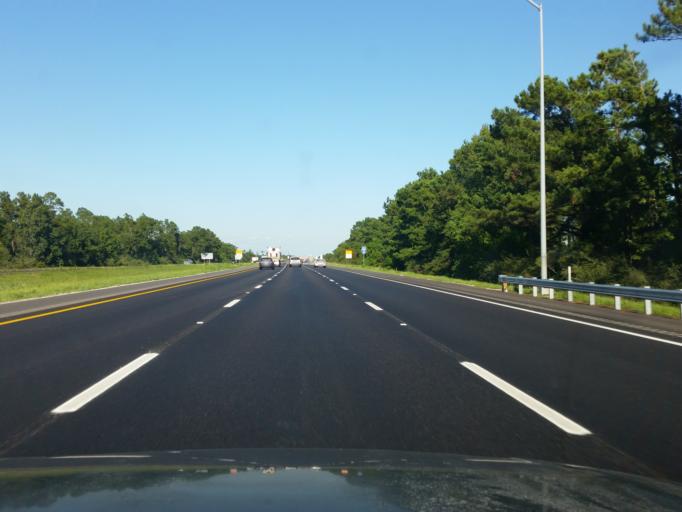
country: US
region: Mississippi
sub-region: Hancock County
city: Kiln
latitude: 30.3601
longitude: -89.4170
